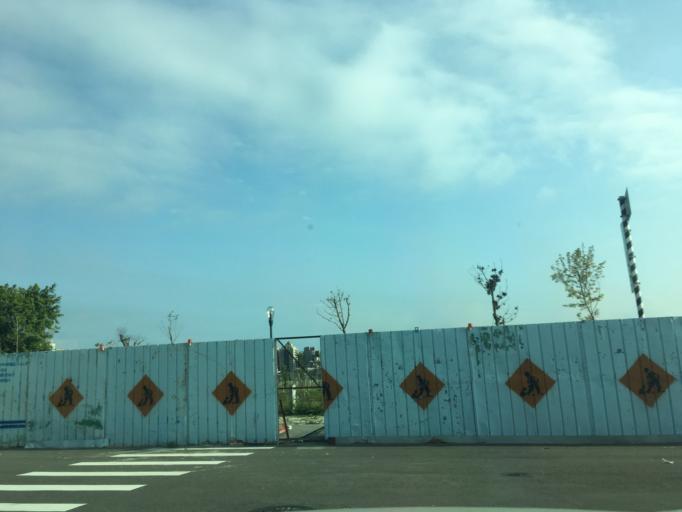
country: TW
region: Taiwan
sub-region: Taichung City
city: Taichung
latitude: 24.1918
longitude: 120.6924
